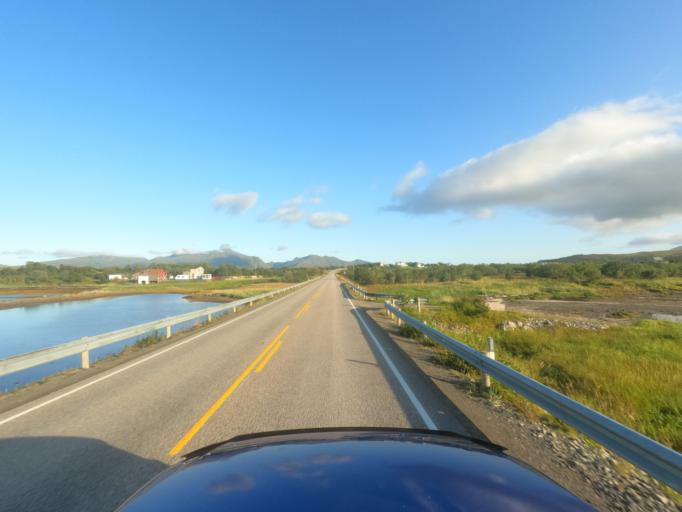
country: NO
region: Nordland
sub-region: Vestvagoy
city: Gravdal
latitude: 68.1534
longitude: 13.5361
